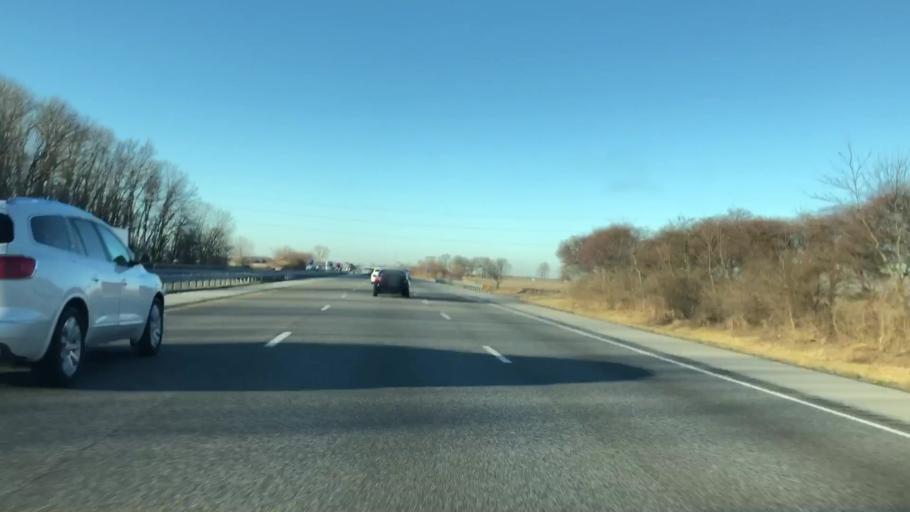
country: US
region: Indiana
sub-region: Johnson County
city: Franklin
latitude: 39.5100
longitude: -86.0211
